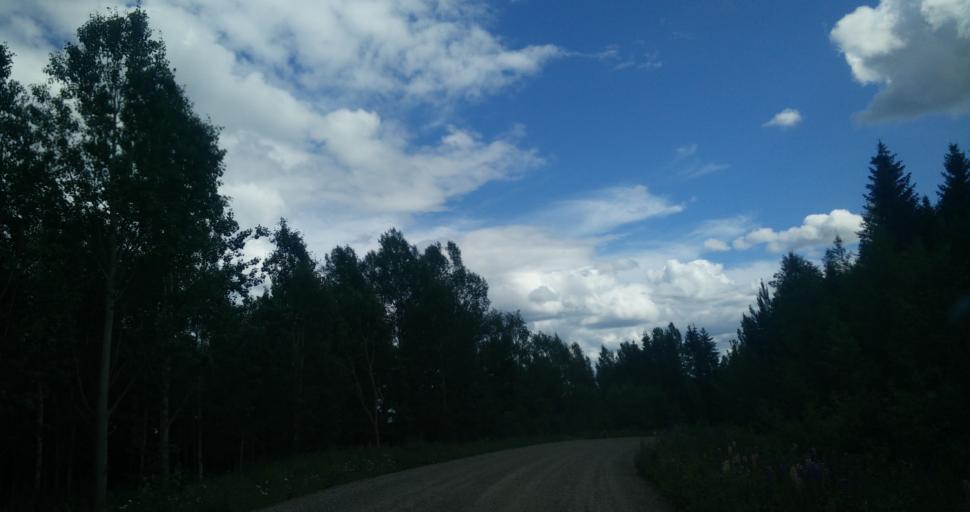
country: SE
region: Gaevleborg
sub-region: Nordanstigs Kommun
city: Bergsjoe
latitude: 62.0661
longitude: 16.7767
